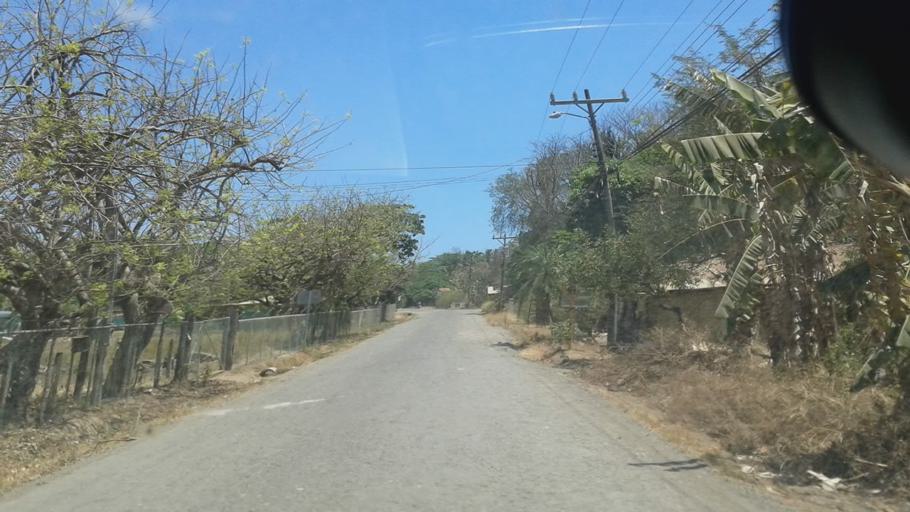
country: CR
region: Guanacaste
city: Samara
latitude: 9.9986
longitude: -85.7040
